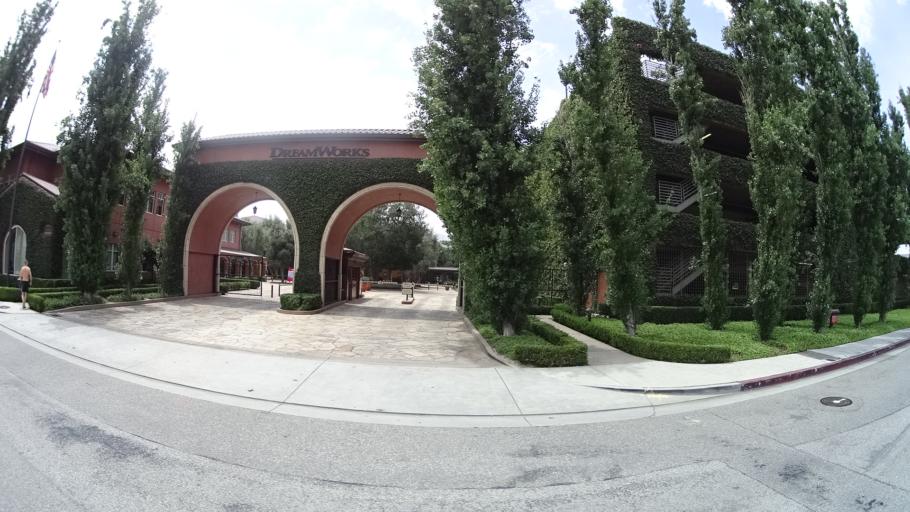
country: US
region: California
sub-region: Los Angeles County
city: North Glendale
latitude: 34.1584
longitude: -118.2854
